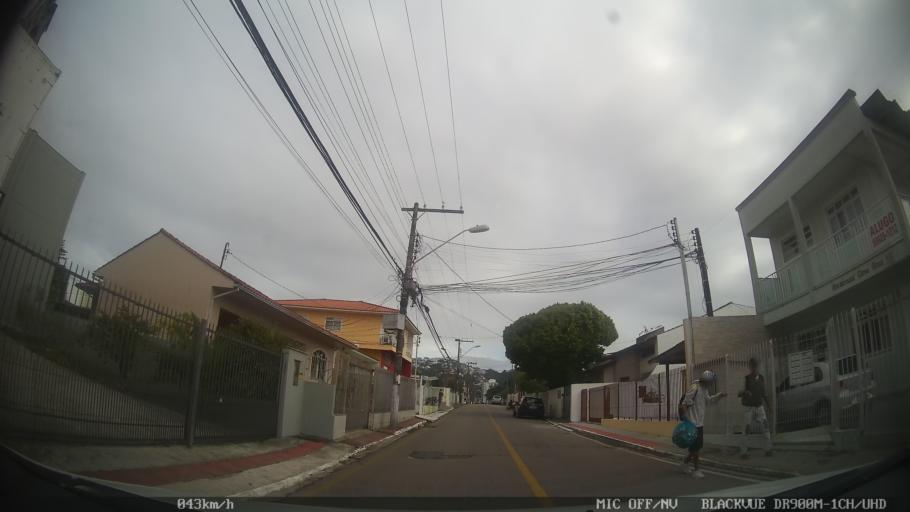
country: BR
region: Santa Catarina
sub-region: Sao Jose
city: Campinas
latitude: -27.5769
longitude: -48.6195
